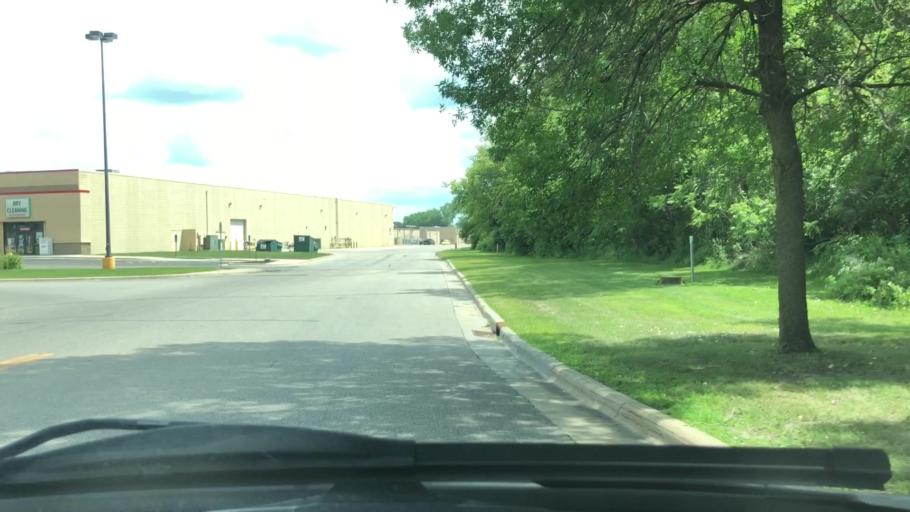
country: US
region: Minnesota
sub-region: Olmsted County
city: Rochester
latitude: 44.0783
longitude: -92.5187
